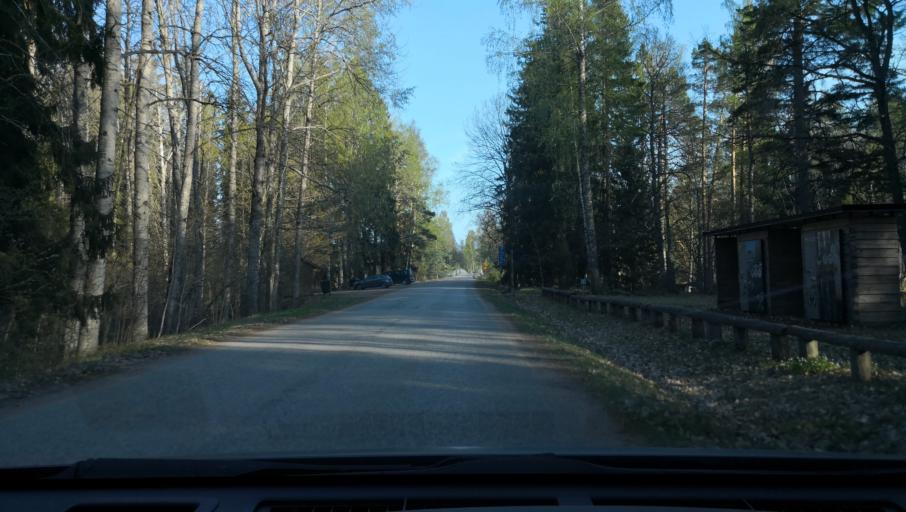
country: SE
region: Uppsala
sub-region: Heby Kommun
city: Tarnsjo
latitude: 60.2707
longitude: 16.9075
